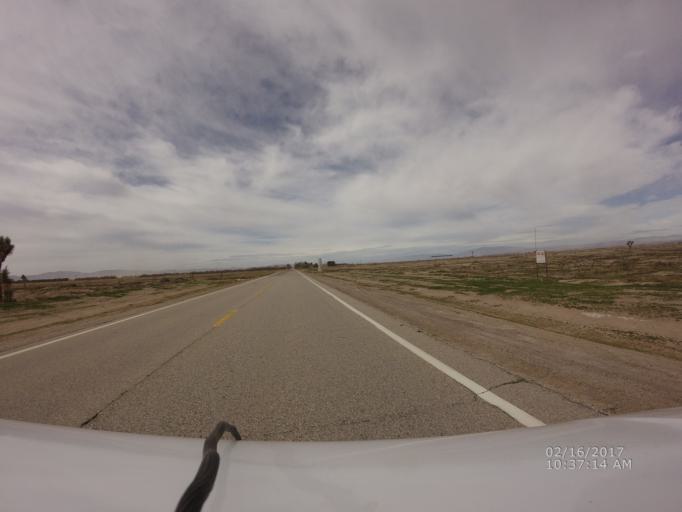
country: US
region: California
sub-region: Los Angeles County
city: Lancaster
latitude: 34.7195
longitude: -117.9913
